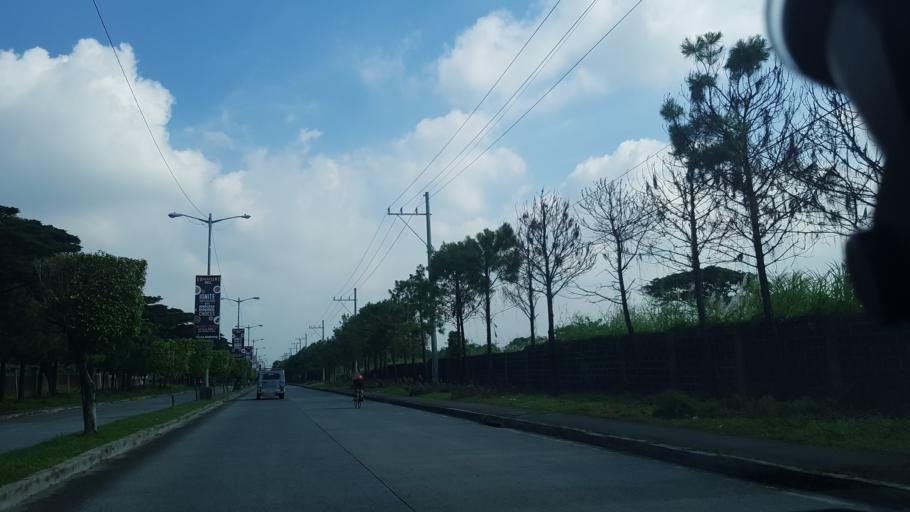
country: PH
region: Calabarzon
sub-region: Province of Laguna
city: Magsaysay
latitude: 14.3574
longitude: 121.0094
